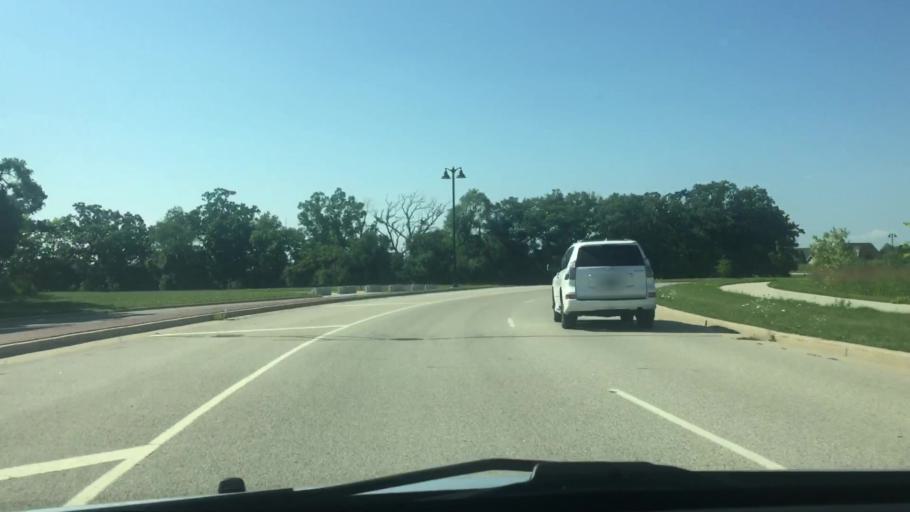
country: US
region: Wisconsin
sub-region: Waukesha County
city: Delafield
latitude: 43.0693
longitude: -88.4570
